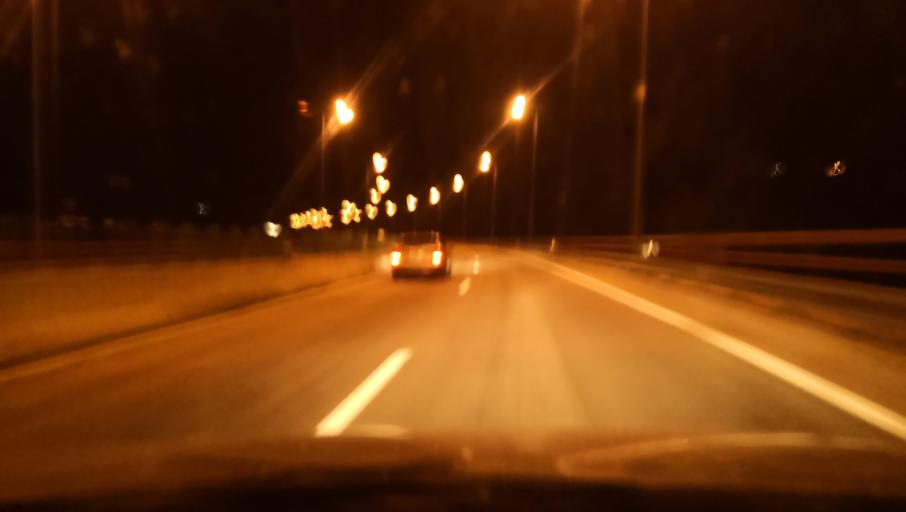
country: ES
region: Castille and Leon
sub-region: Provincia de Zamora
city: Trabazos
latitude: 41.7432
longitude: -6.5612
